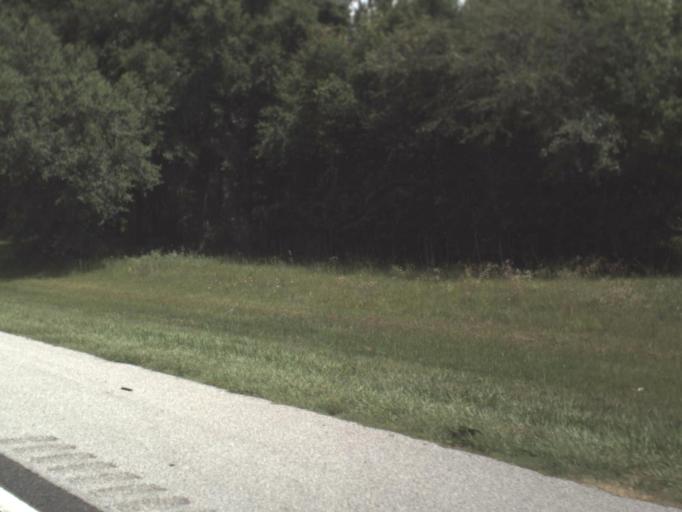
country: US
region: Florida
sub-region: Suwannee County
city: Wellborn
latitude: 30.3156
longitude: -82.8051
